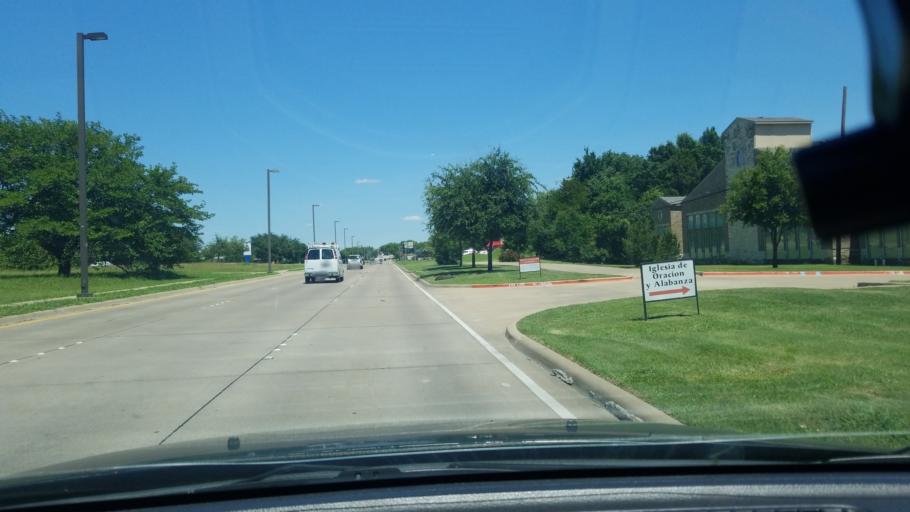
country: US
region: Texas
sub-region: Dallas County
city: Mesquite
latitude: 32.7672
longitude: -96.6123
